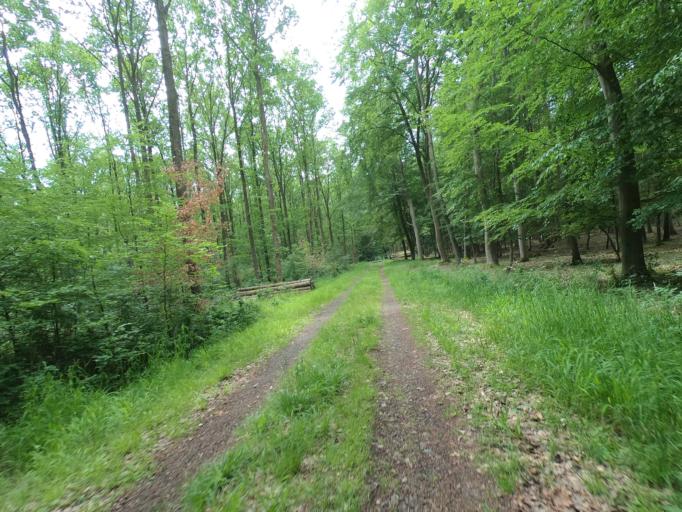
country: DE
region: Hesse
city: Morfelden-Walldorf
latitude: 49.9765
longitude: 8.5250
